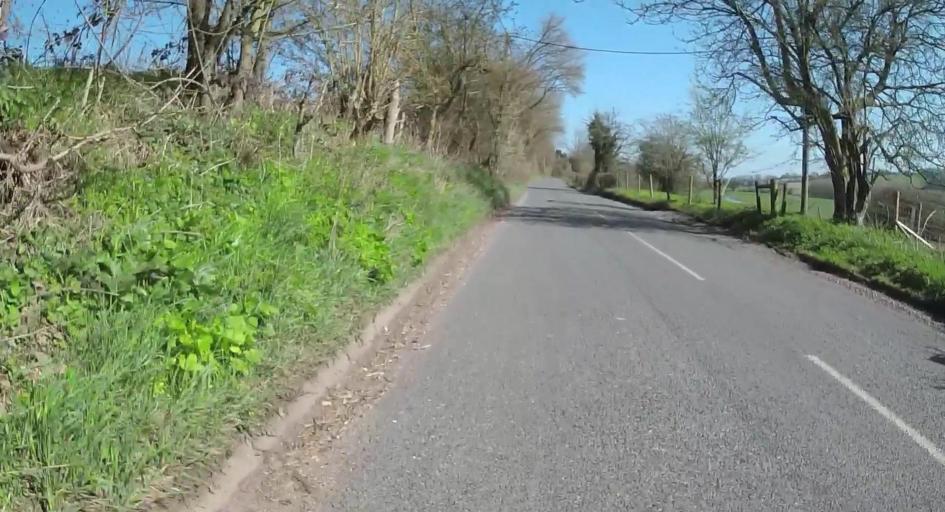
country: GB
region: England
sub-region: Hampshire
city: Andover
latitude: 51.2741
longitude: -1.4464
